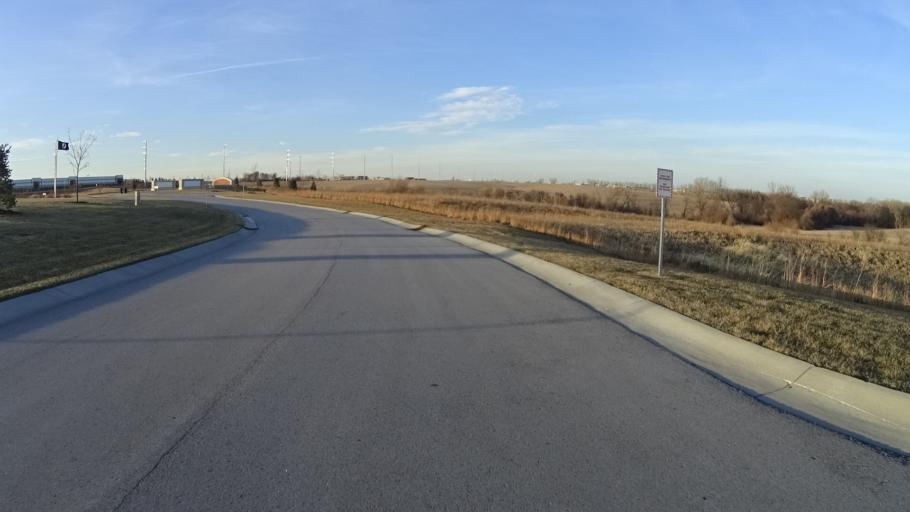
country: US
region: Nebraska
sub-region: Sarpy County
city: Chalco
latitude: 41.1388
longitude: -96.1320
